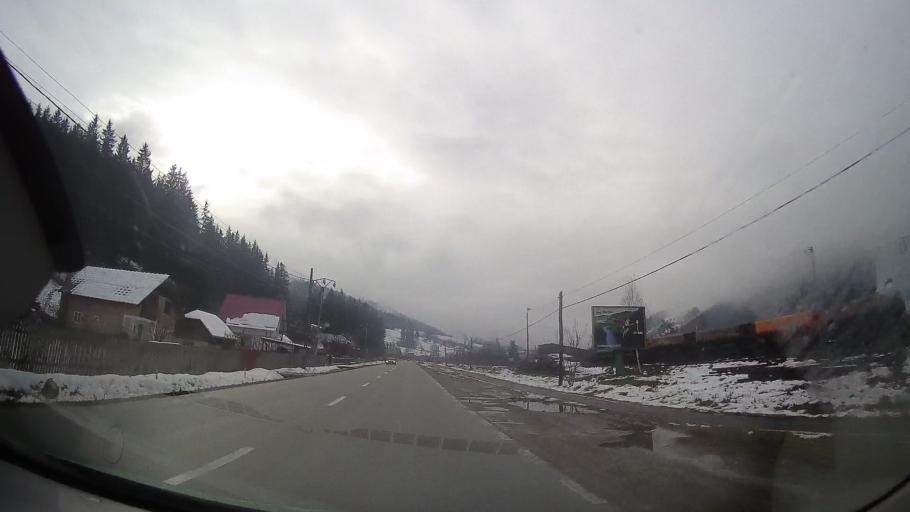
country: RO
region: Neamt
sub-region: Comuna Tasca
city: Tasca
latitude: 46.8920
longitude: 26.0183
